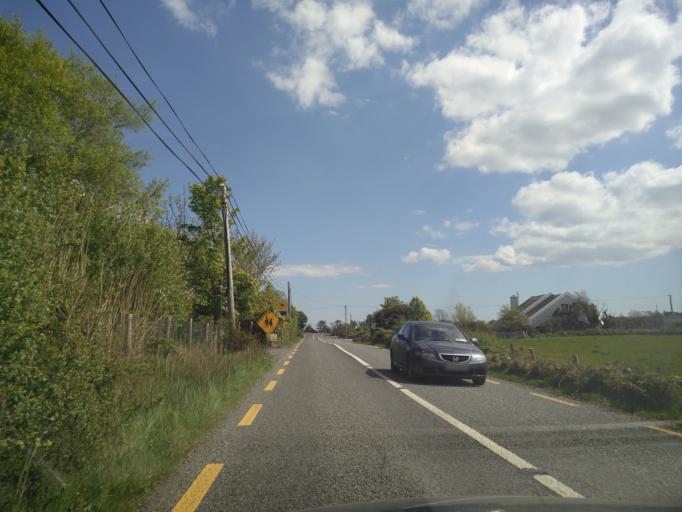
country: IE
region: Connaught
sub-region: Maigh Eo
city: Westport
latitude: 53.7837
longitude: -9.4477
